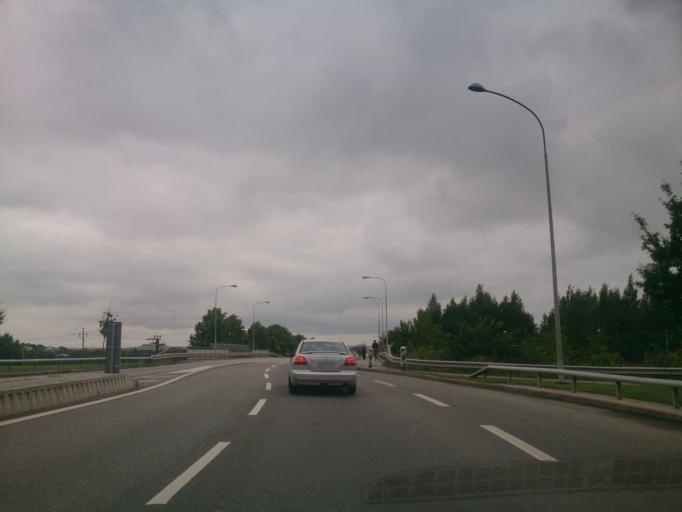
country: SE
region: OEstergoetland
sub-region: Linkopings Kommun
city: Linkoping
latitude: 58.4208
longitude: 15.5956
